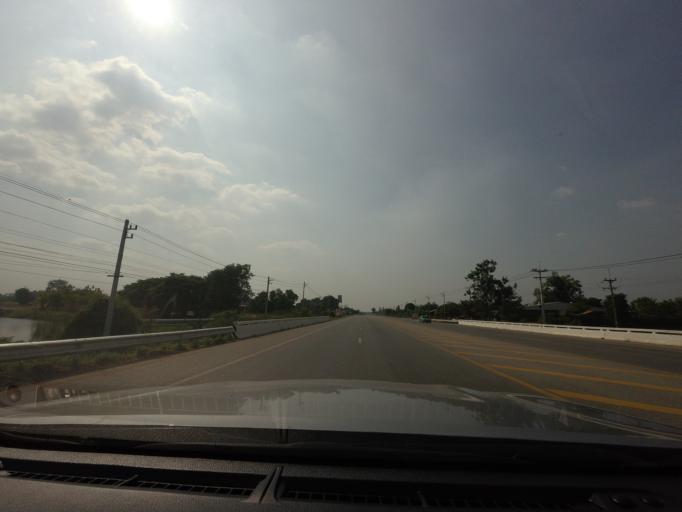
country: TH
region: Phitsanulok
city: Bang Rakam
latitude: 16.7665
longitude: 100.1401
